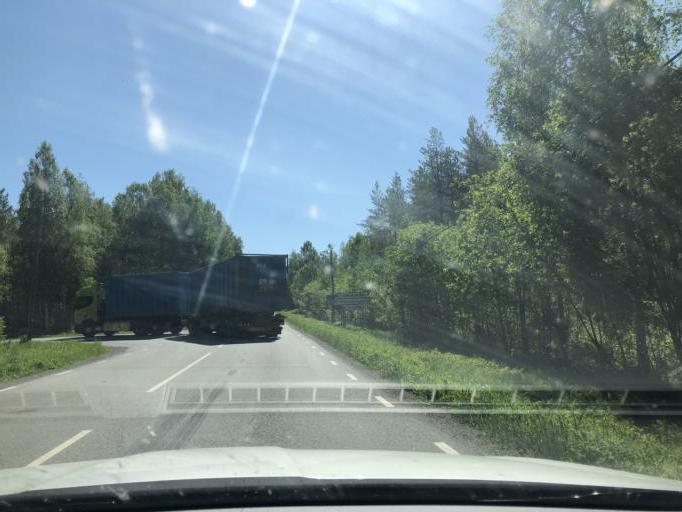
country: SE
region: Norrbotten
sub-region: Lulea Kommun
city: Sodra Sunderbyn
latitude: 65.6639
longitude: 21.9696
